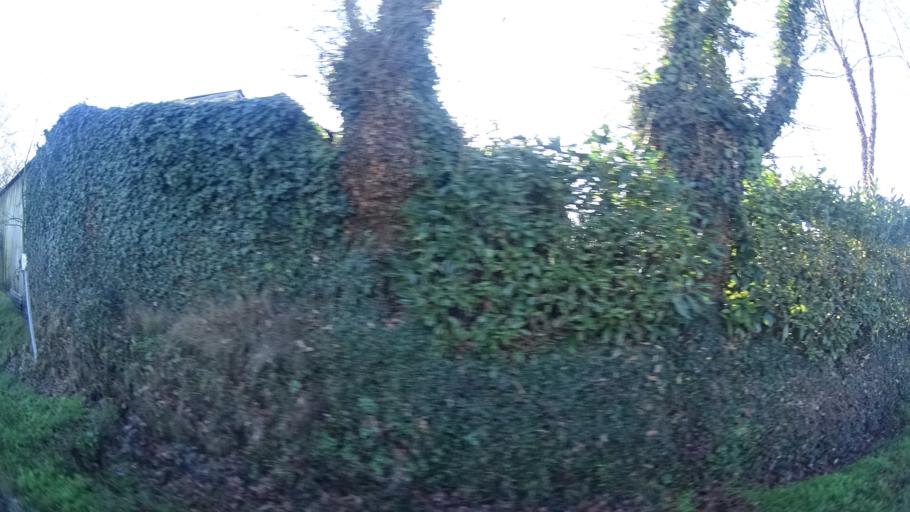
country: FR
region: Brittany
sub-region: Departement du Morbihan
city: Saint-Jean-la-Poterie
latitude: 47.6483
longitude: -2.1366
